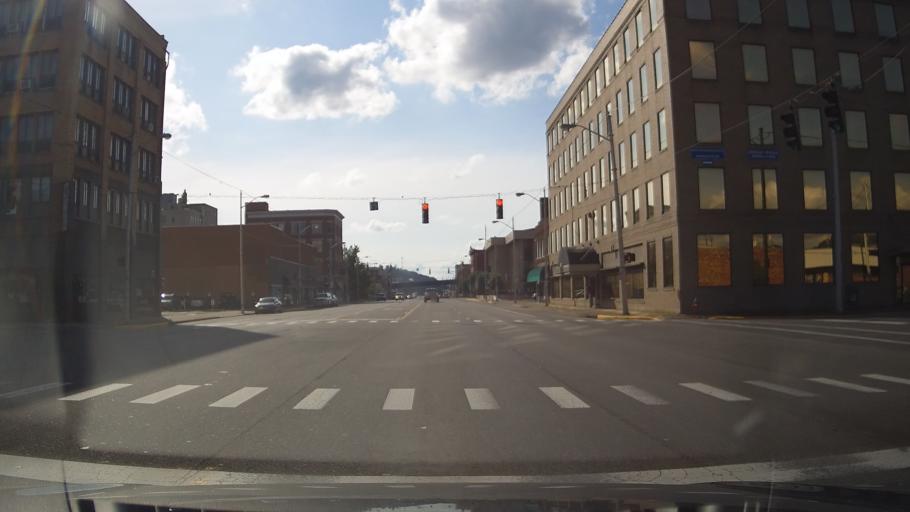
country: US
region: Kentucky
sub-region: Boyd County
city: Ashland
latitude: 38.4795
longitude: -82.6386
